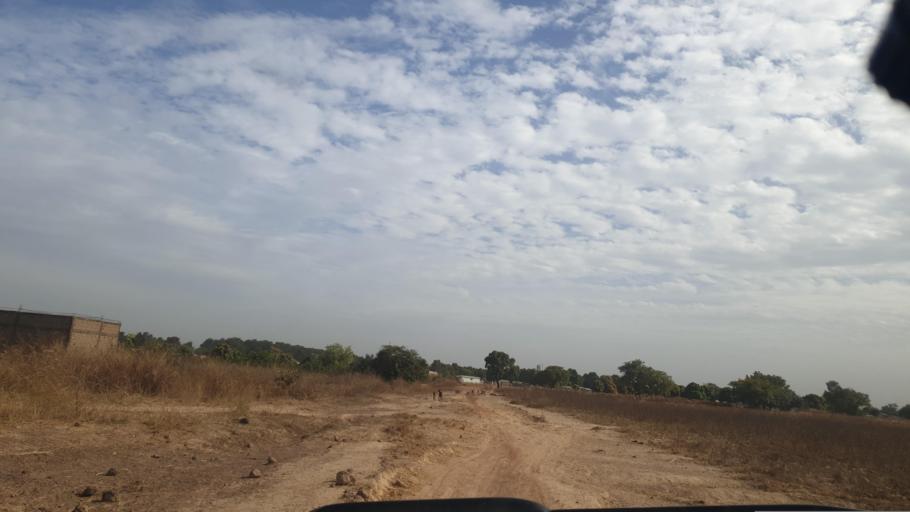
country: ML
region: Sikasso
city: Yanfolila
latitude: 11.4130
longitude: -8.0040
